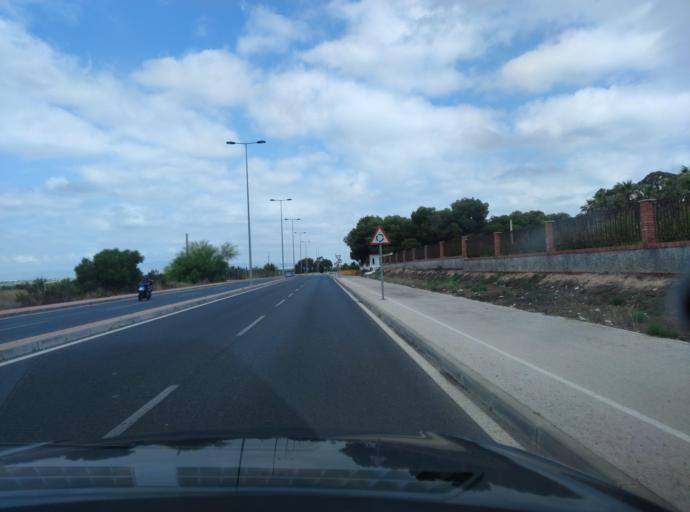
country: ES
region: Valencia
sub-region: Provincia de Alicante
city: Santa Pola
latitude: 38.2080
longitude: -0.5845
